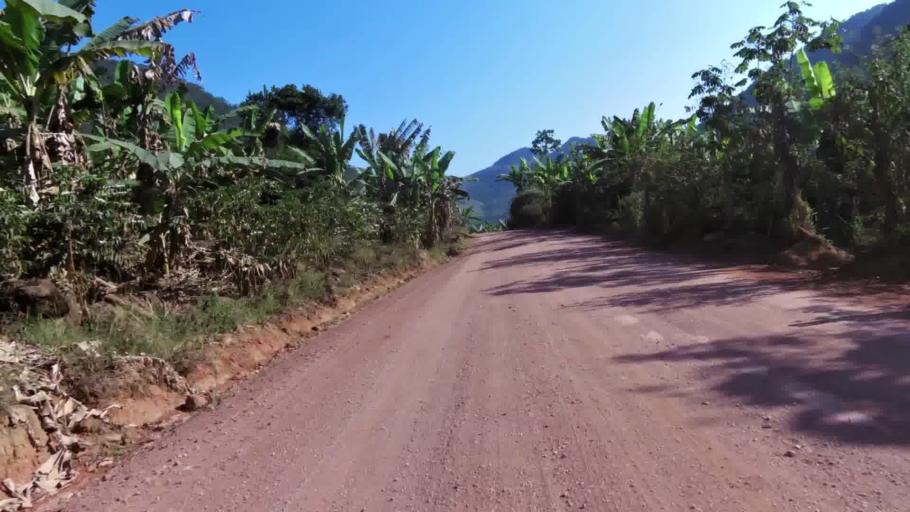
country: BR
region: Espirito Santo
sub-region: Alfredo Chaves
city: Alfredo Chaves
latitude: -20.6017
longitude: -40.7624
